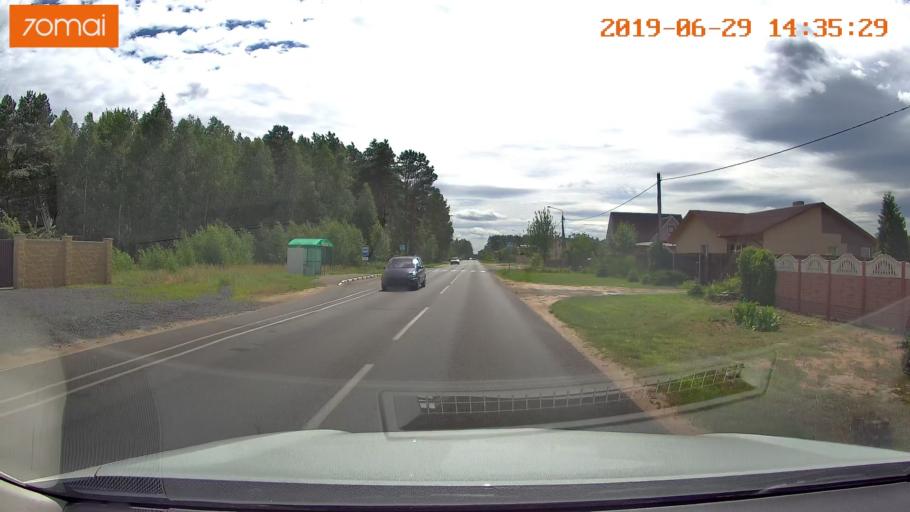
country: BY
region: Minsk
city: Starobin
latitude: 52.7596
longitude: 27.4856
